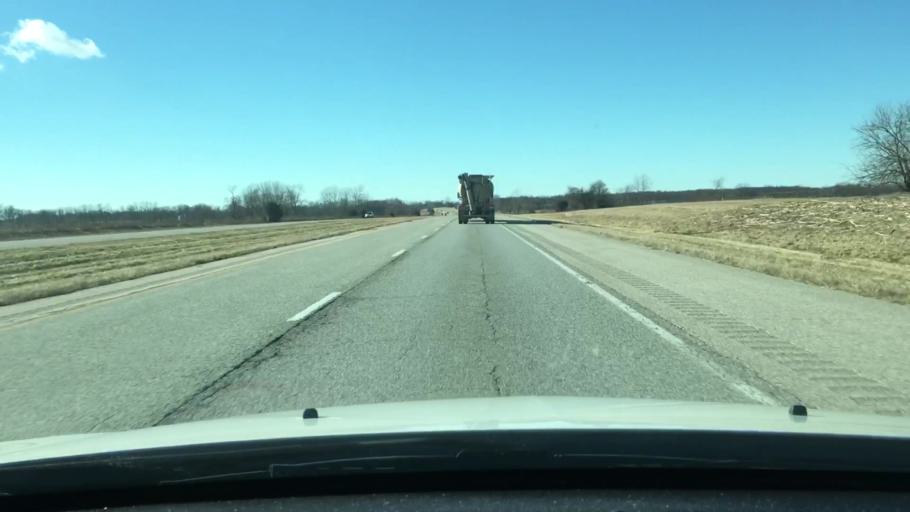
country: US
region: Illinois
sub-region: Pike County
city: Griggsville
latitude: 39.6784
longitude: -90.7083
